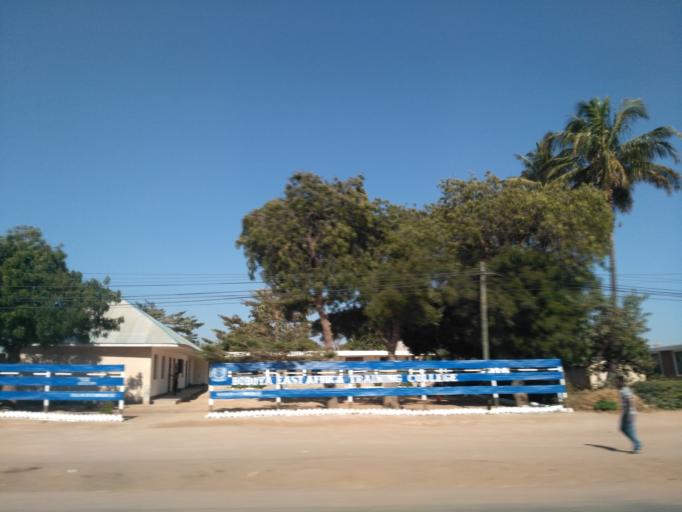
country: TZ
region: Dodoma
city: Dodoma
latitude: -6.1403
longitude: 35.7467
